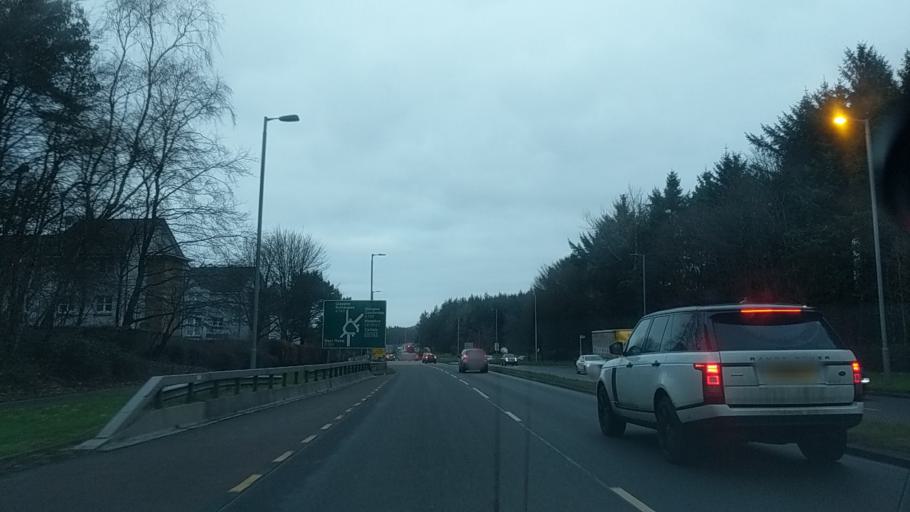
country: GB
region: Scotland
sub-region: South Lanarkshire
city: East Kilbride
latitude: 55.7737
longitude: -4.1636
